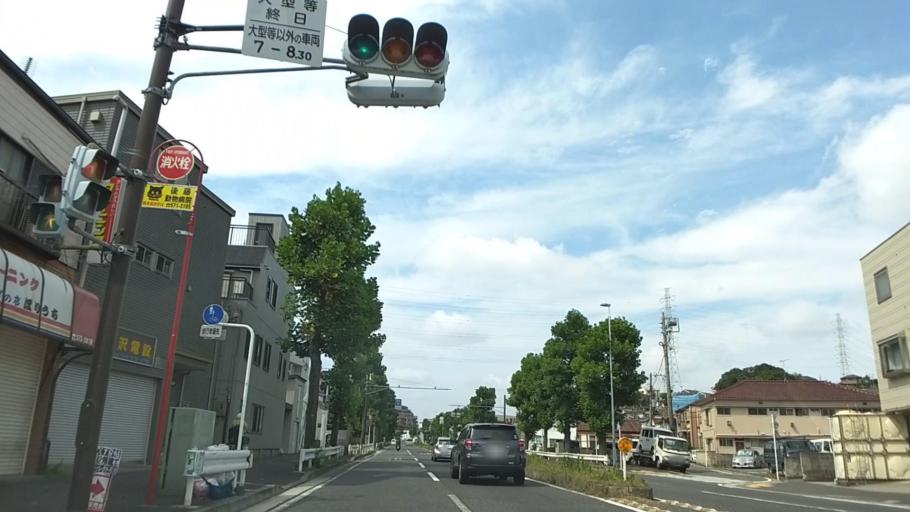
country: JP
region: Kanagawa
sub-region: Kawasaki-shi
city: Kawasaki
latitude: 35.5311
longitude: 139.6638
